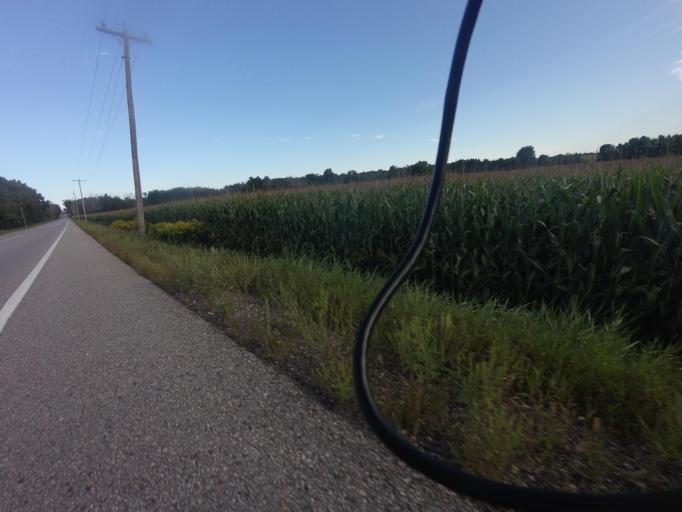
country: CA
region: Ontario
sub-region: Wellington County
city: Guelph
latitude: 43.5820
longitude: -80.3384
